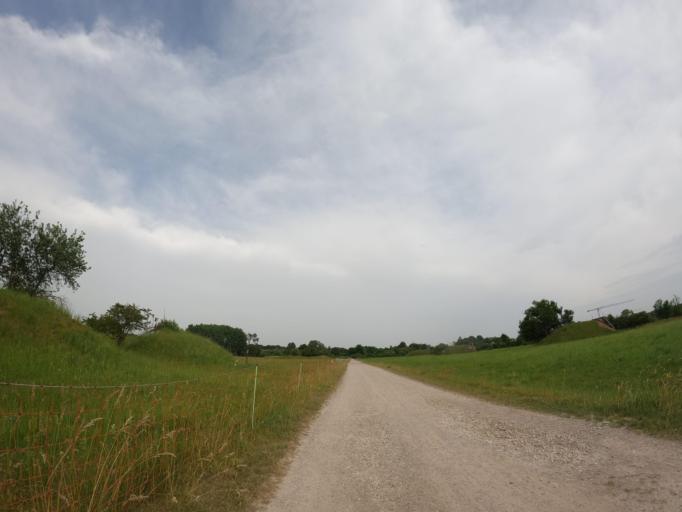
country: DE
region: Bavaria
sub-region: Upper Bavaria
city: Neubiberg
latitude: 48.0677
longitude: 11.6462
